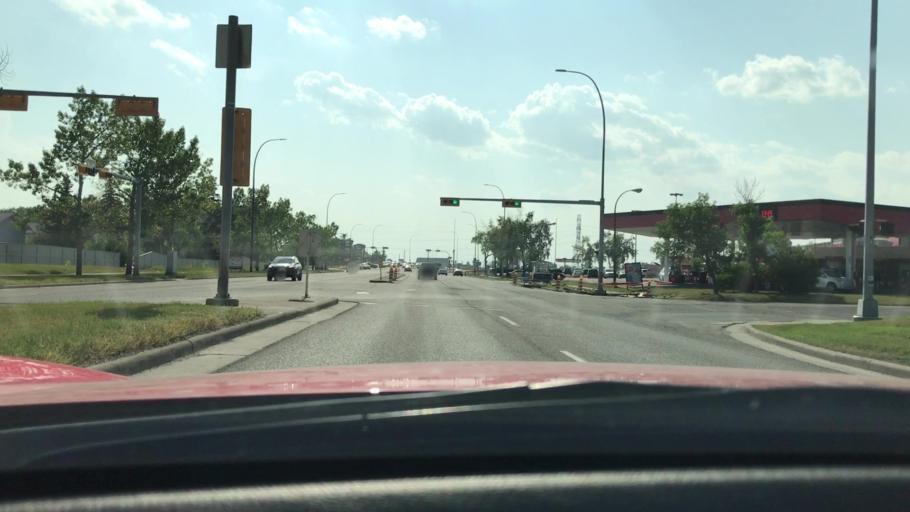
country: CA
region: Alberta
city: Calgary
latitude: 51.0184
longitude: -114.1562
